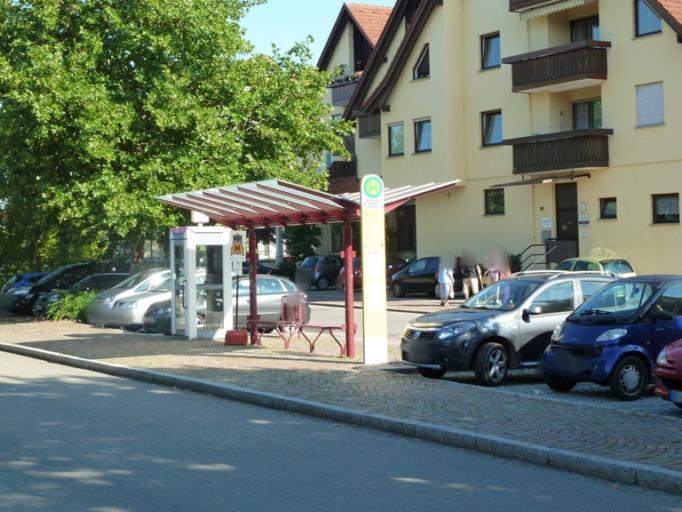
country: DE
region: Baden-Wuerttemberg
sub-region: Tuebingen Region
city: Kressbronn am Bodensee
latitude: 47.5946
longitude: 9.5989
